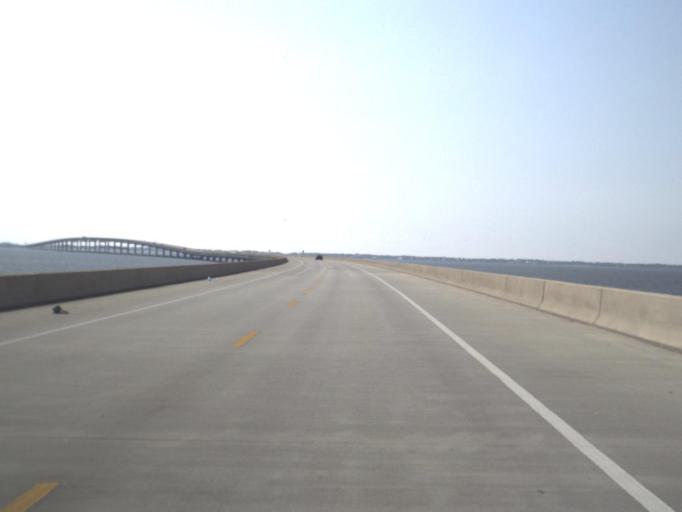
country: US
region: Florida
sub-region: Franklin County
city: Eastpoint
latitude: 29.6966
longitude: -84.8893
